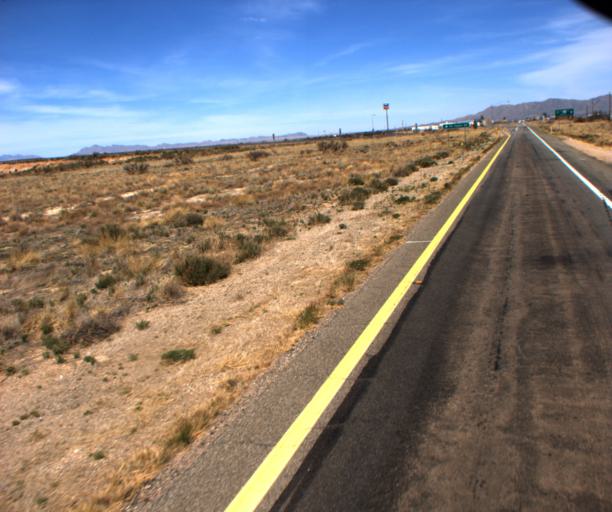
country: US
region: Arizona
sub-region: Cochise County
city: Willcox
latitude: 32.2192
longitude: -109.8779
